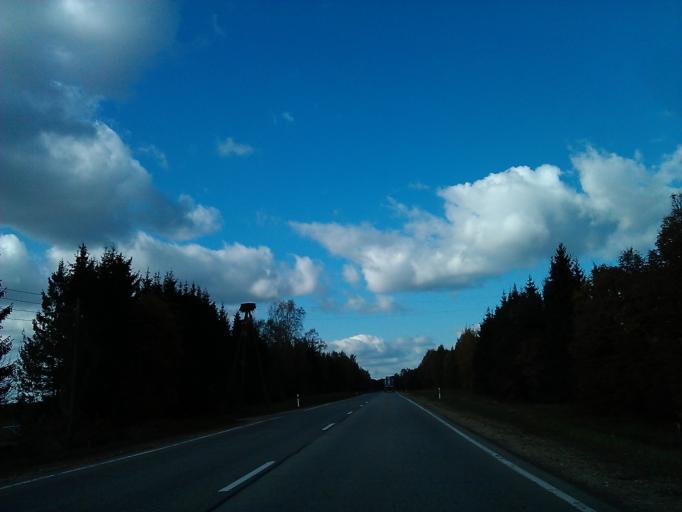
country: LV
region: Livani
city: Livani
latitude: 56.4482
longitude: 26.0625
